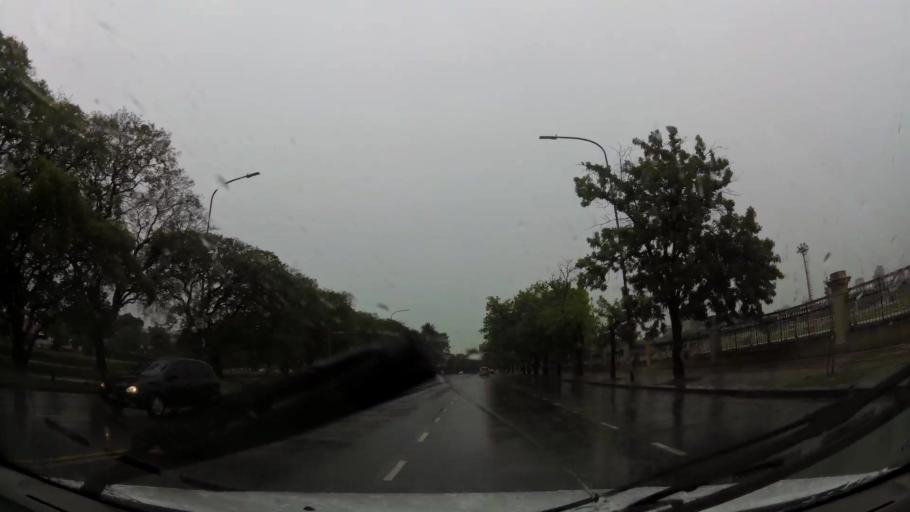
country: AR
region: Buenos Aires F.D.
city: Colegiales
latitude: -34.5673
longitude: -58.4212
